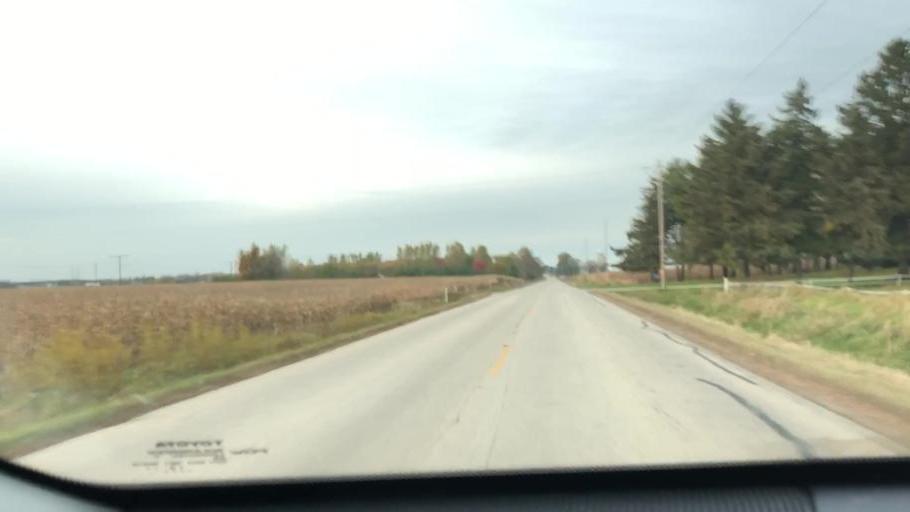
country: US
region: Wisconsin
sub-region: Outagamie County
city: Seymour
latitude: 44.4515
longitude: -88.3502
